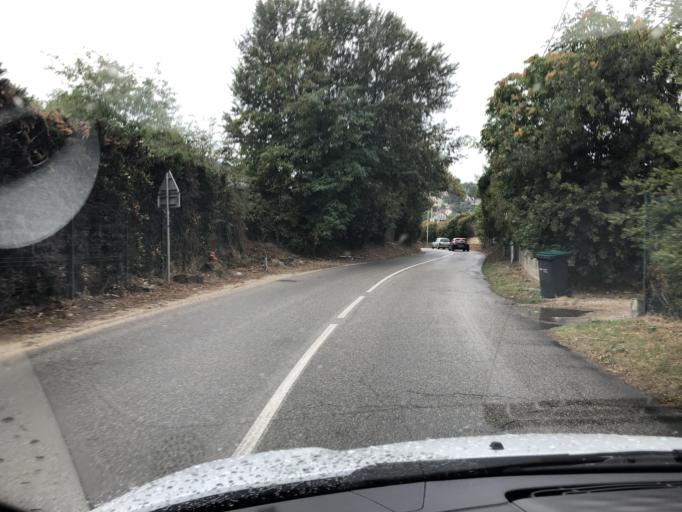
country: FR
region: Provence-Alpes-Cote d'Azur
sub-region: Departement des Bouches-du-Rhone
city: La Penne-sur-Huveaune
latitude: 43.2829
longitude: 5.5237
